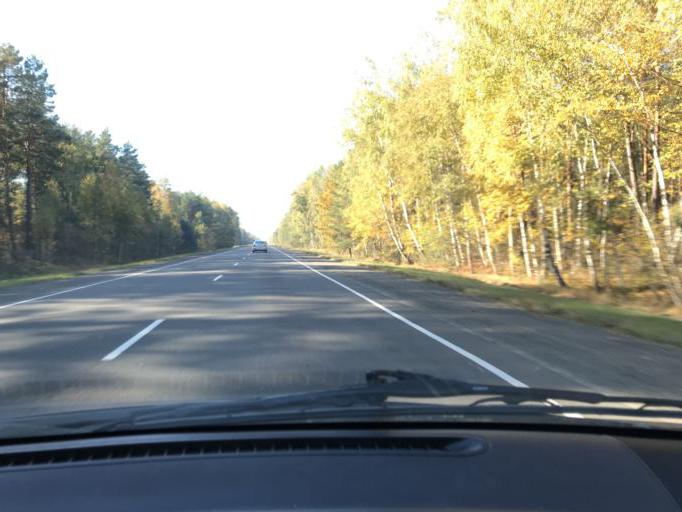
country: BY
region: Brest
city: Asnyezhytsy
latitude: 52.2574
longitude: 26.2938
